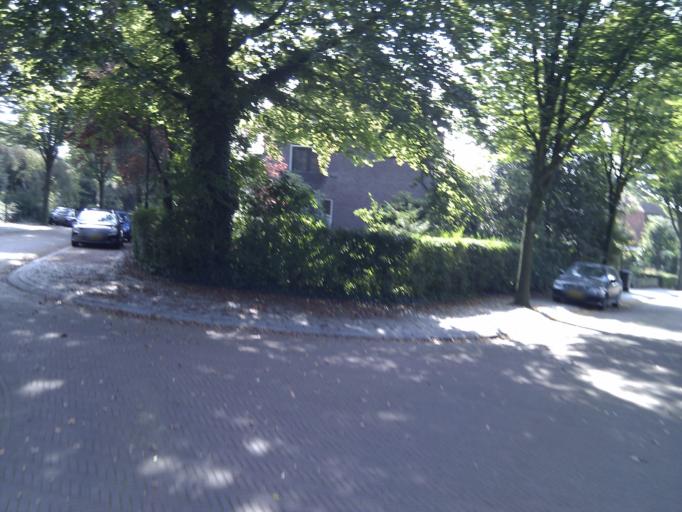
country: NL
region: Utrecht
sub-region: Gemeente De Bilt
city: De Bilt
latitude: 52.1274
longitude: 5.1992
